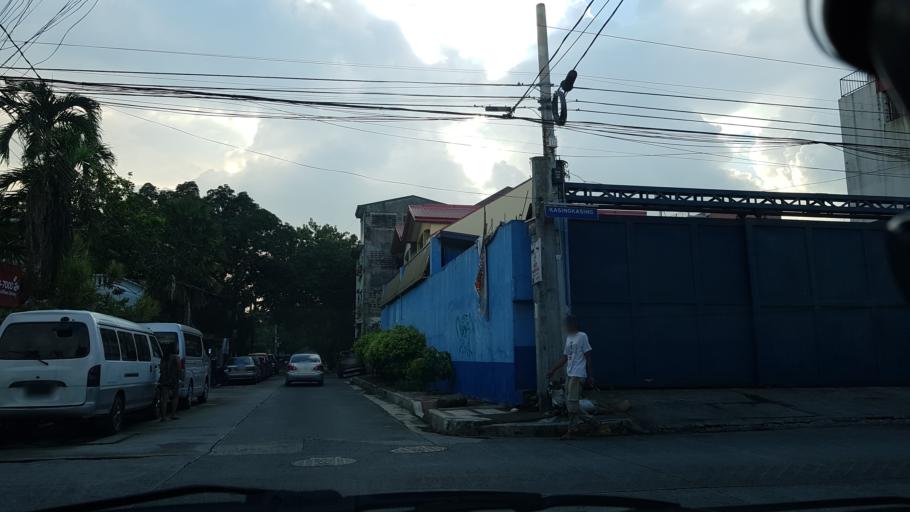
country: PH
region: Metro Manila
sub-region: Quezon City
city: Quezon City
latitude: 14.6329
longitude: 121.0570
